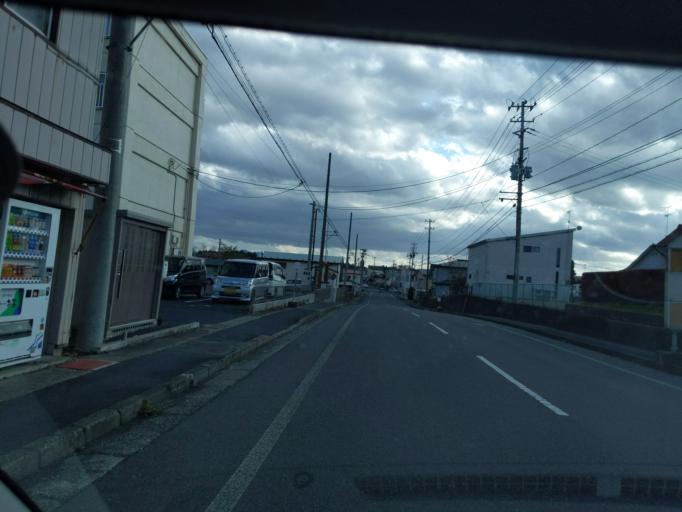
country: JP
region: Iwate
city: Mizusawa
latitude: 39.1320
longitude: 141.1412
